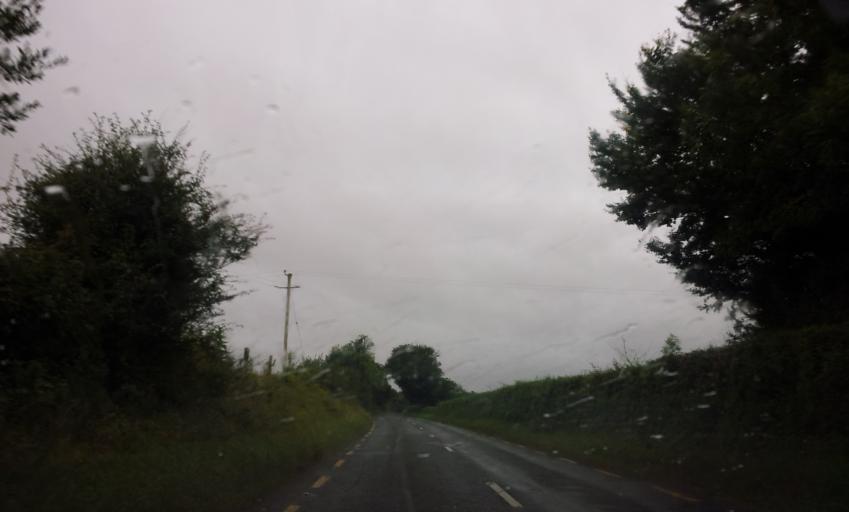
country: IE
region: Munster
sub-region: County Cork
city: Mallow
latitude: 52.1899
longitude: -8.5291
